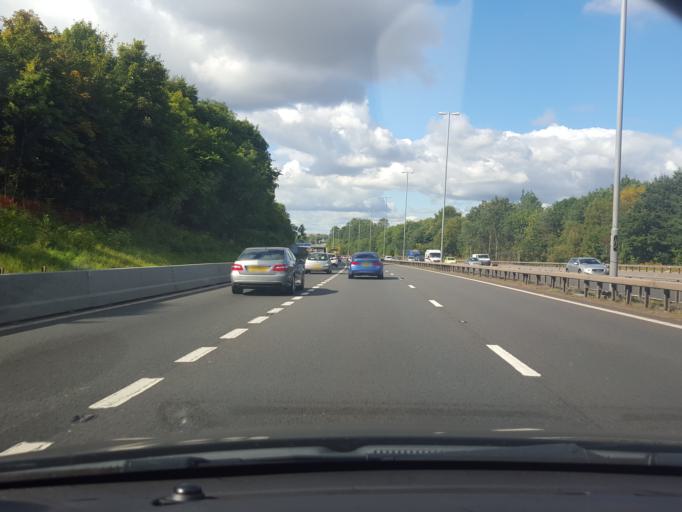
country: GB
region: Scotland
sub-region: South Lanarkshire
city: Uddingston
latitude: 55.8259
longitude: -4.0809
